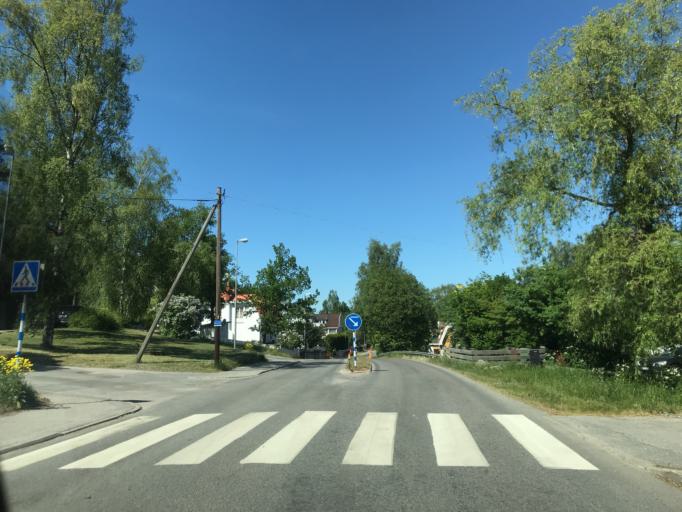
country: SE
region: Stockholm
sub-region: Sollentuna Kommun
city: Sollentuna
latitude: 59.4158
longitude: 17.9727
